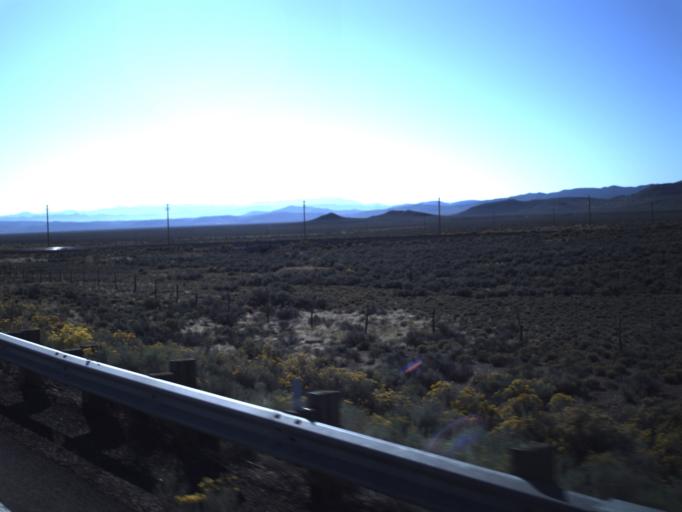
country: US
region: Utah
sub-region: Washington County
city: Enterprise
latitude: 37.8024
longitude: -113.9196
